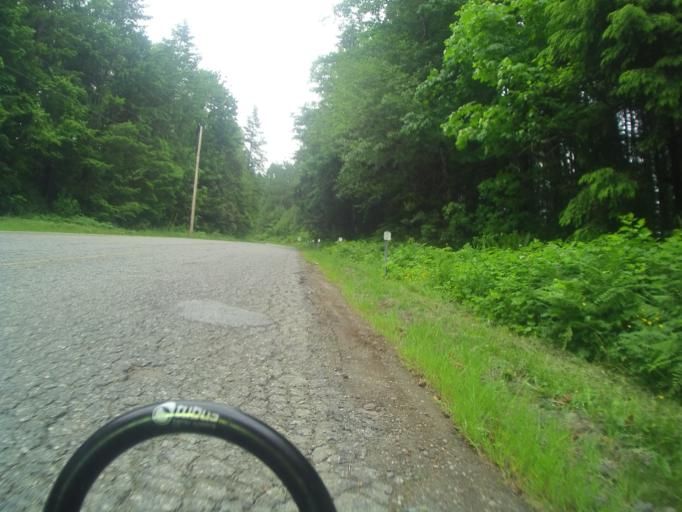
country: CA
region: British Columbia
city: Agassiz
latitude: 49.3157
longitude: -121.8919
